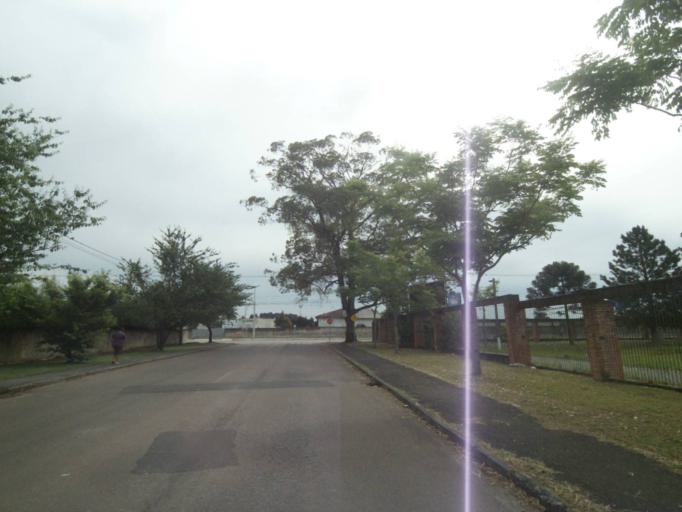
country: BR
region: Parana
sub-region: Pinhais
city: Pinhais
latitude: -25.4213
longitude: -49.2164
